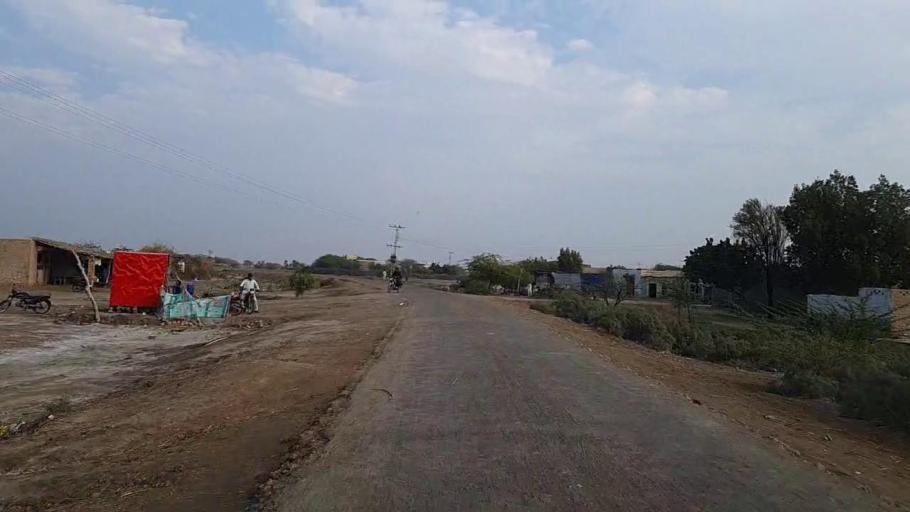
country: PK
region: Sindh
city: Pithoro
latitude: 25.4513
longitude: 69.2853
